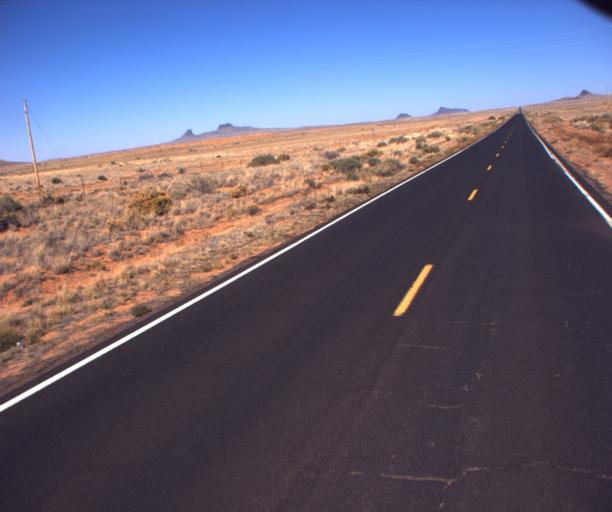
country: US
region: Arizona
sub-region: Navajo County
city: Dilkon
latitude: 35.3313
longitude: -110.4235
